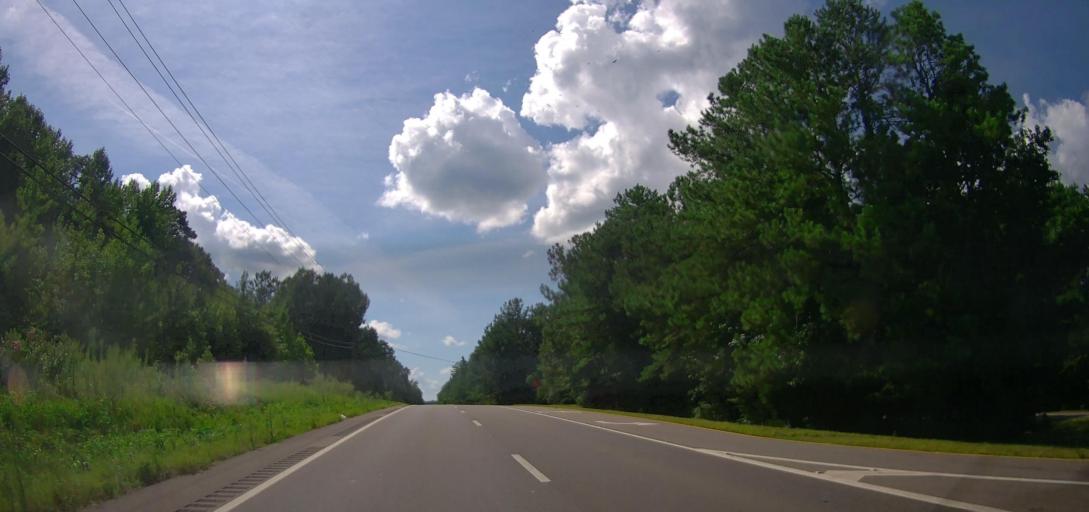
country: US
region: Alabama
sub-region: Tuscaloosa County
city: Northport
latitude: 33.2406
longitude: -87.6626
